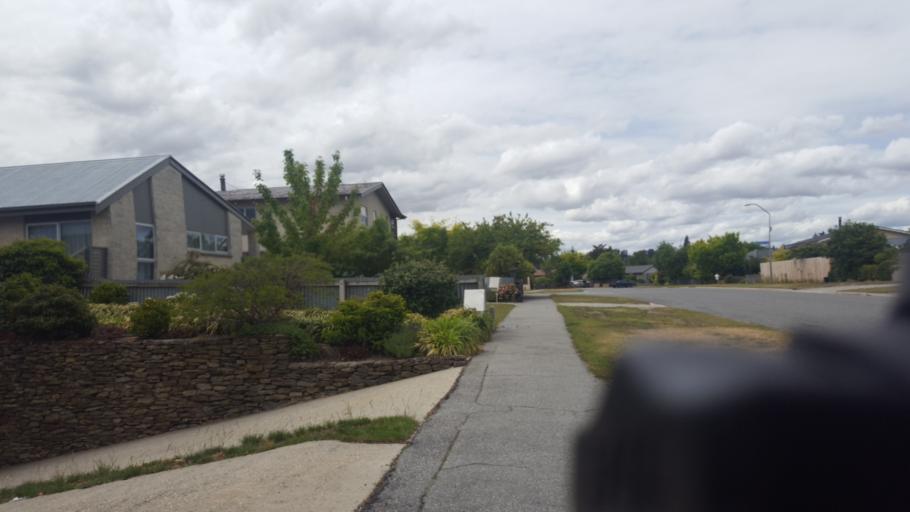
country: NZ
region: Otago
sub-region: Queenstown-Lakes District
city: Wanaka
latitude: -45.2459
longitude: 169.3781
